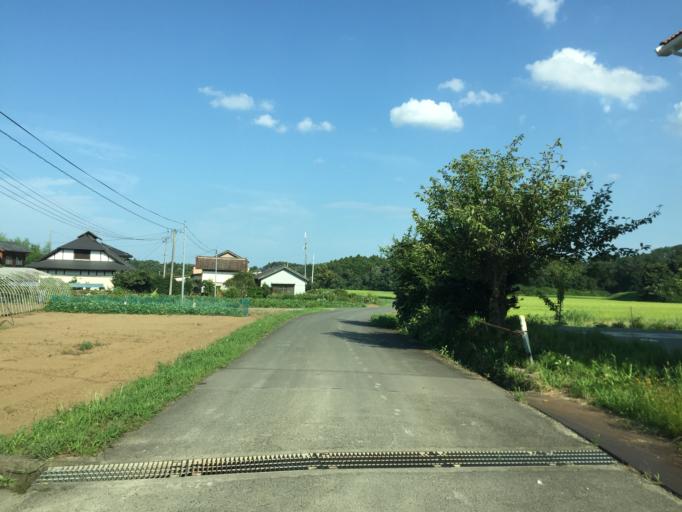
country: JP
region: Miyagi
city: Marumori
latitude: 37.8004
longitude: 140.8985
